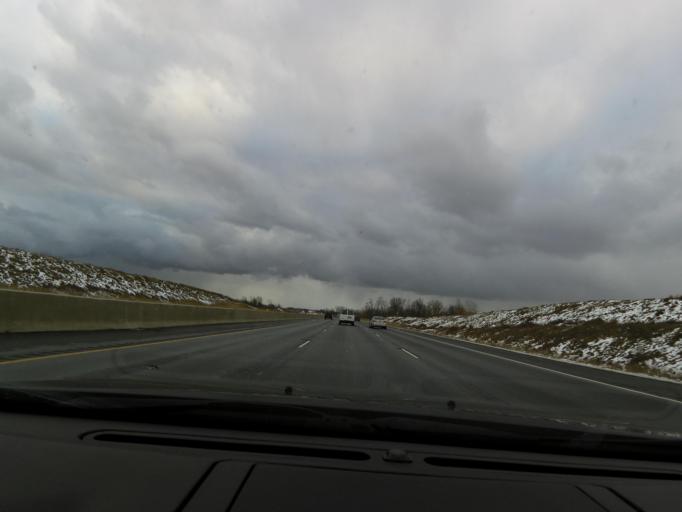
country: CA
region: Ontario
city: Burlington
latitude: 43.3970
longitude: -79.8338
